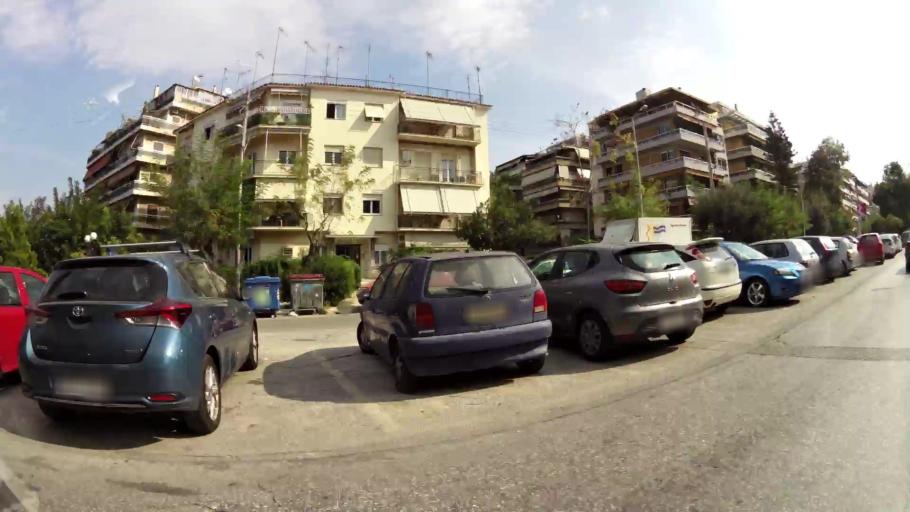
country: GR
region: Attica
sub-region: Nomarchia Athinas
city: Nea Smyrni
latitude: 37.9514
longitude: 23.7161
